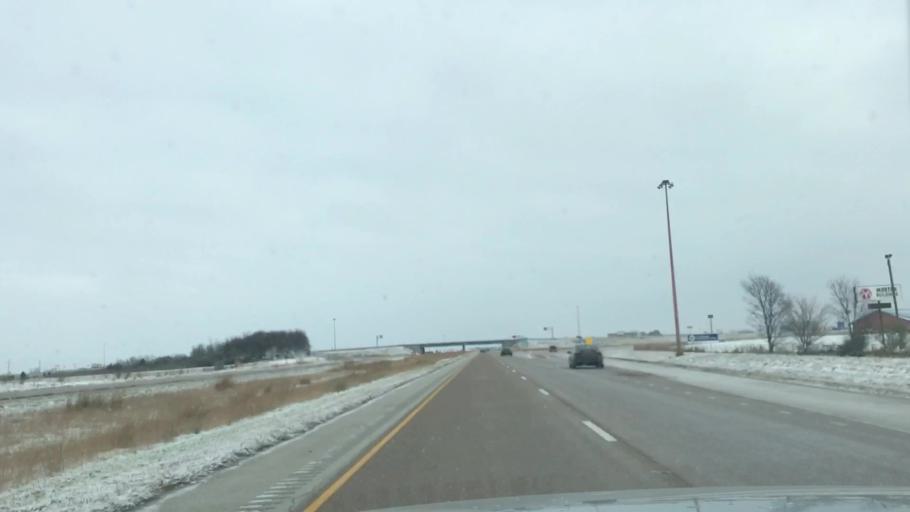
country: US
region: Illinois
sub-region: Montgomery County
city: Litchfield
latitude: 39.1700
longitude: -89.6843
